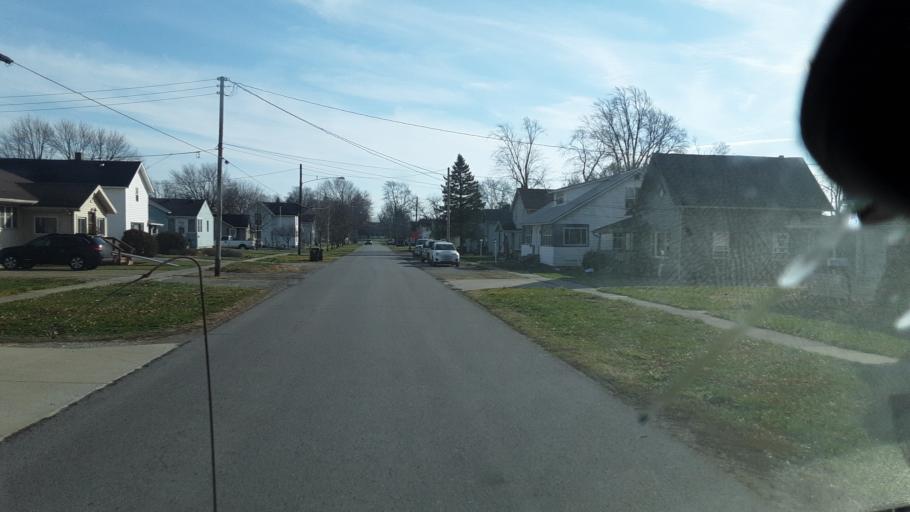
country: US
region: Ohio
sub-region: Defiance County
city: Hicksville
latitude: 41.2921
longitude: -84.7699
